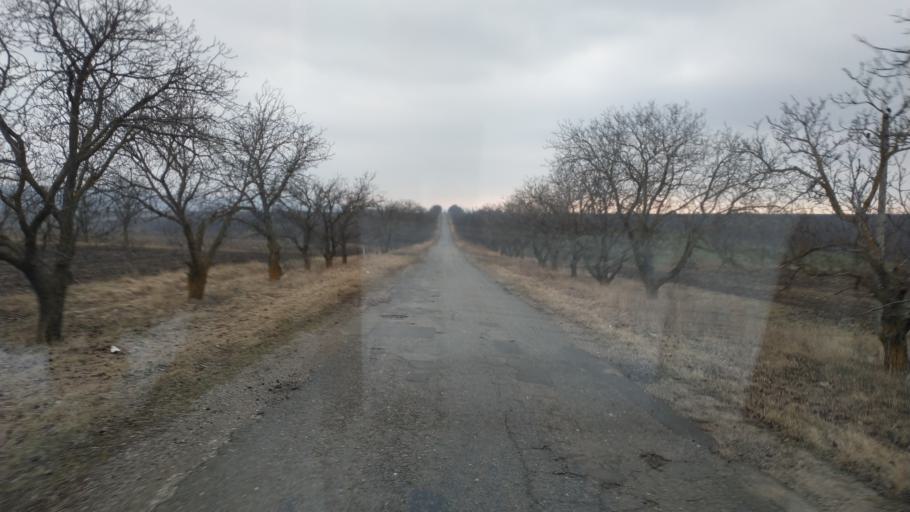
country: MD
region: Hincesti
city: Dancu
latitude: 46.8752
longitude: 28.2962
